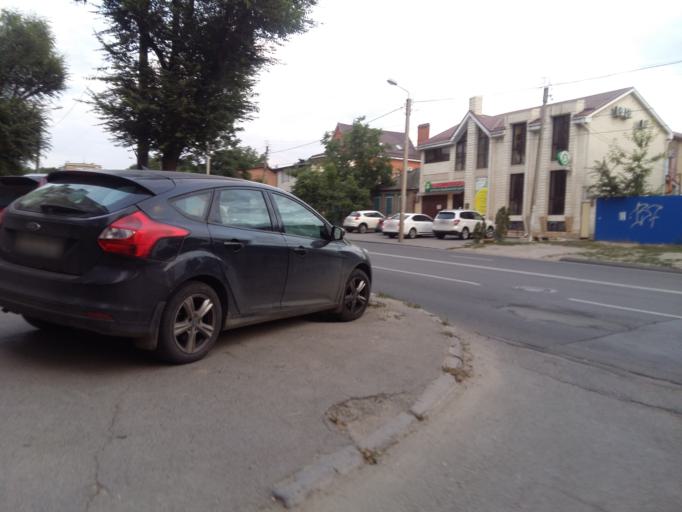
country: RU
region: Rostov
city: Imeni Chkalova
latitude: 47.2751
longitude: 39.7392
